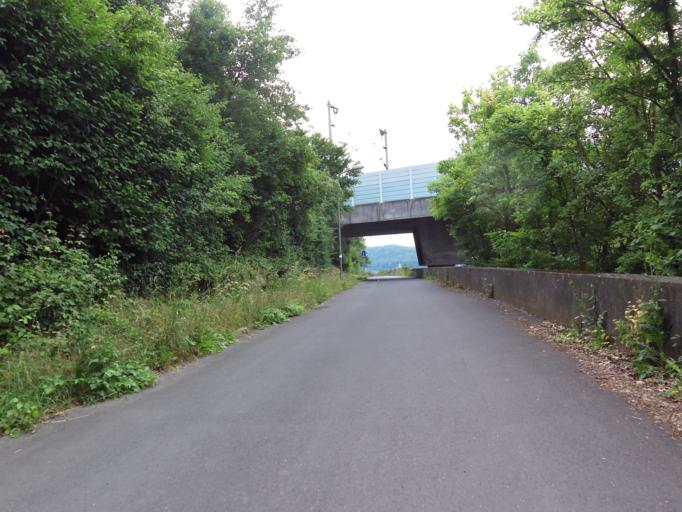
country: DE
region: Bavaria
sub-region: Regierungsbezirk Unterfranken
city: Veitshochheim
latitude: 49.8223
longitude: 9.8788
